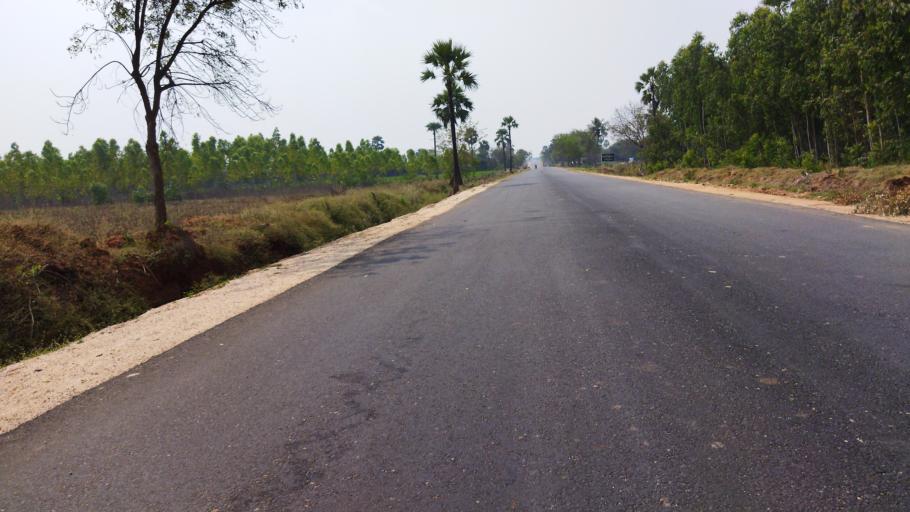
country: IN
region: Telangana
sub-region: Nalgonda
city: Nalgonda
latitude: 17.1526
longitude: 79.4072
